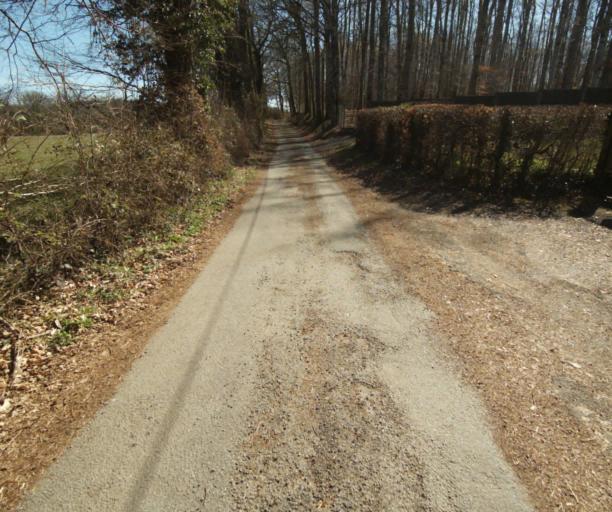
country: FR
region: Limousin
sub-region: Departement de la Correze
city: Chamboulive
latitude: 45.4565
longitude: 1.7287
